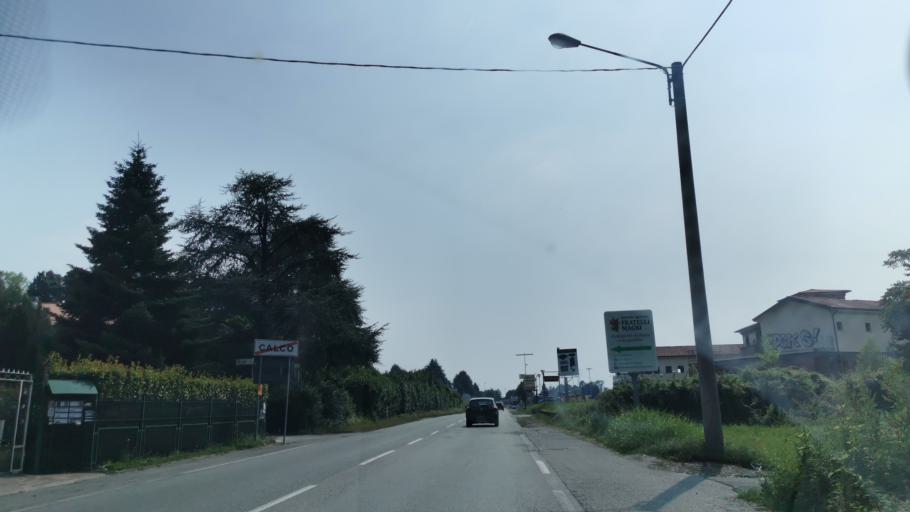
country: IT
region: Lombardy
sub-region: Provincia di Lecco
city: Calco
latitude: 45.7201
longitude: 9.4111
